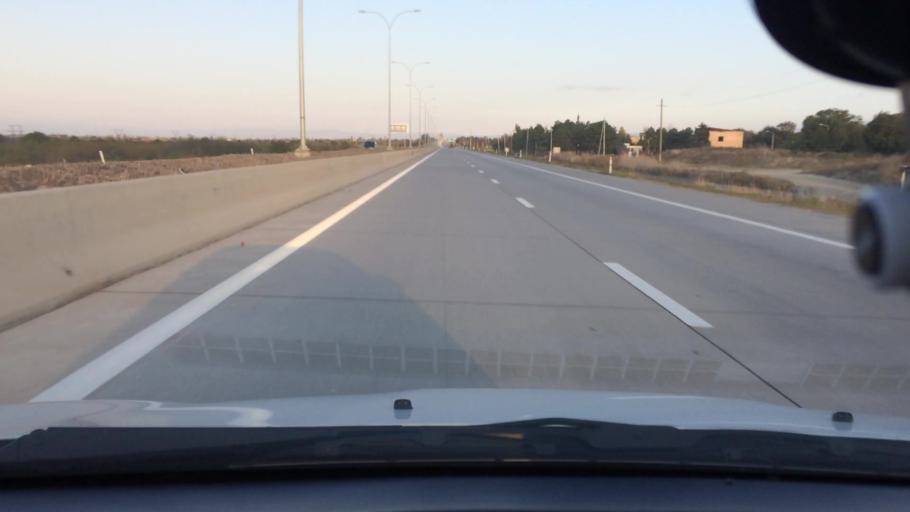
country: GE
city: Agara
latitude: 42.0246
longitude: 43.9688
